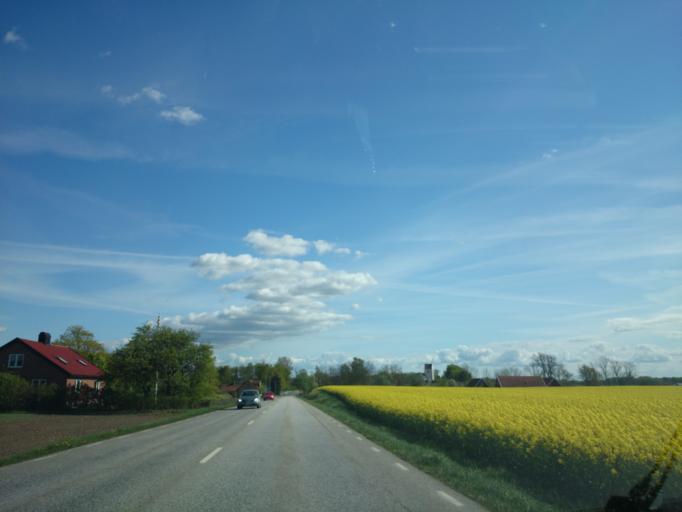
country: SE
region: Skane
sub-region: Lunds Kommun
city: Lund
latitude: 55.7452
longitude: 13.1703
